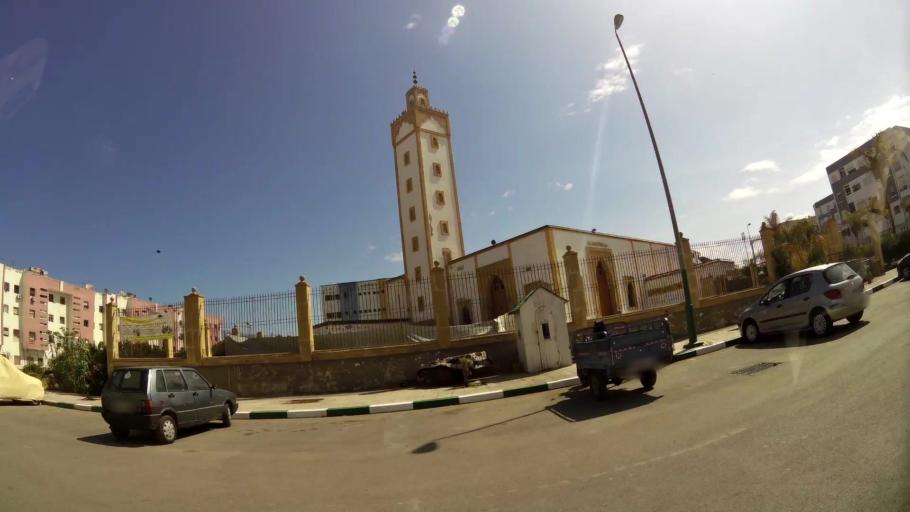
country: MA
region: Rabat-Sale-Zemmour-Zaer
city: Sale
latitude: 34.0813
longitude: -6.7877
